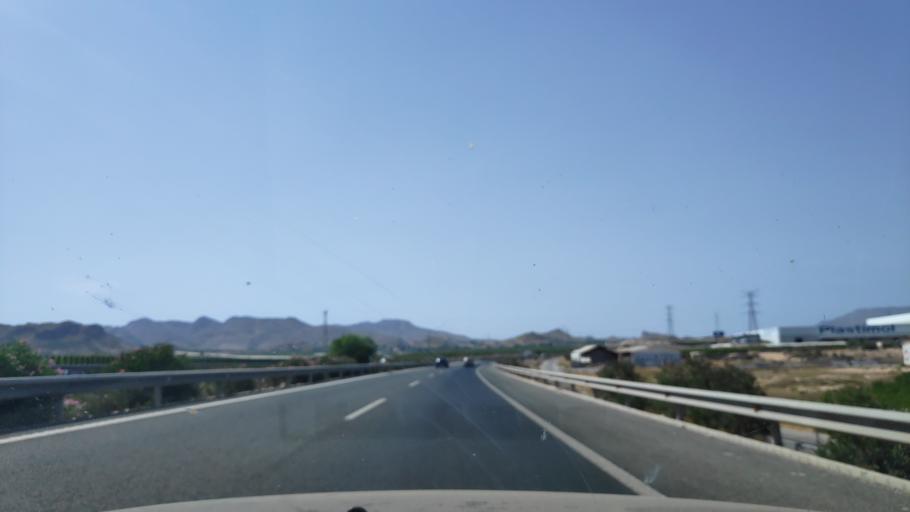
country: ES
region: Murcia
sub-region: Murcia
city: Archena
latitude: 38.1338
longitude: -1.2680
